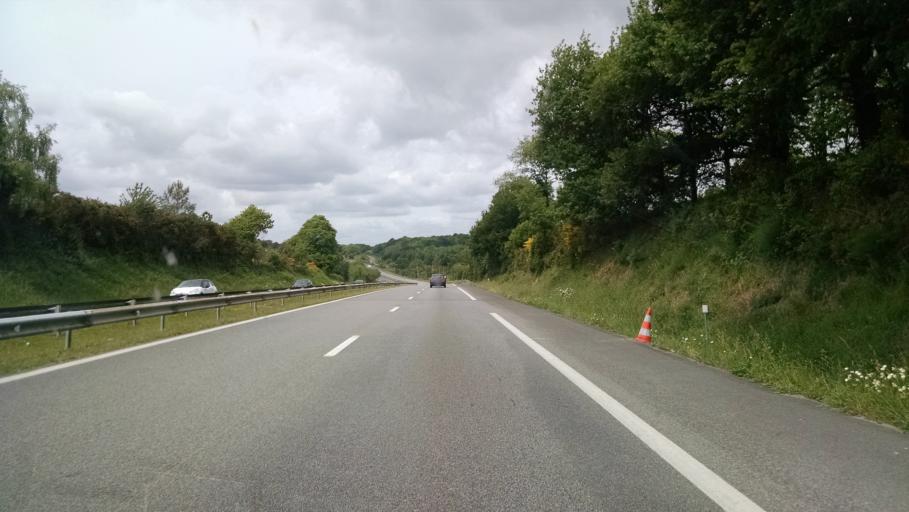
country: FR
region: Brittany
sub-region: Departement du Morbihan
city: Muzillac
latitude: 47.5458
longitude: -2.4385
